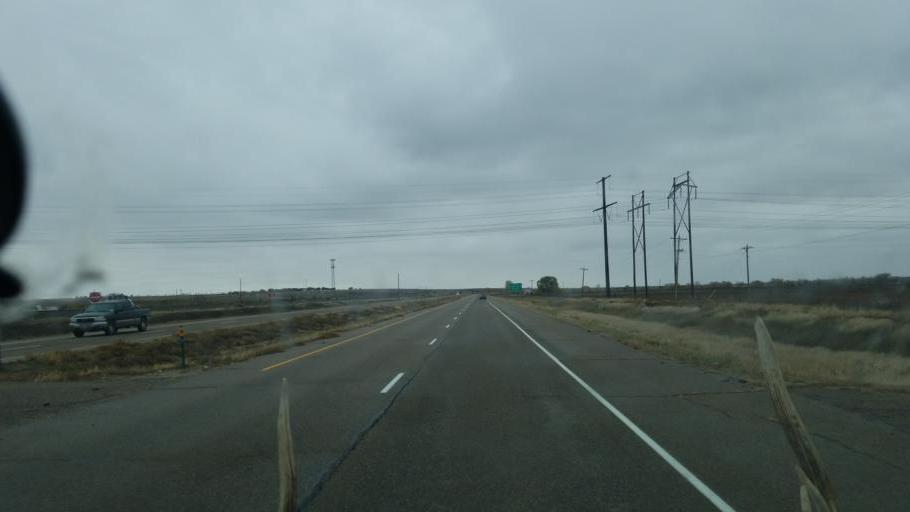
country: US
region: Colorado
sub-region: Pueblo County
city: Pueblo
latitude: 38.2682
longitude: -104.3875
